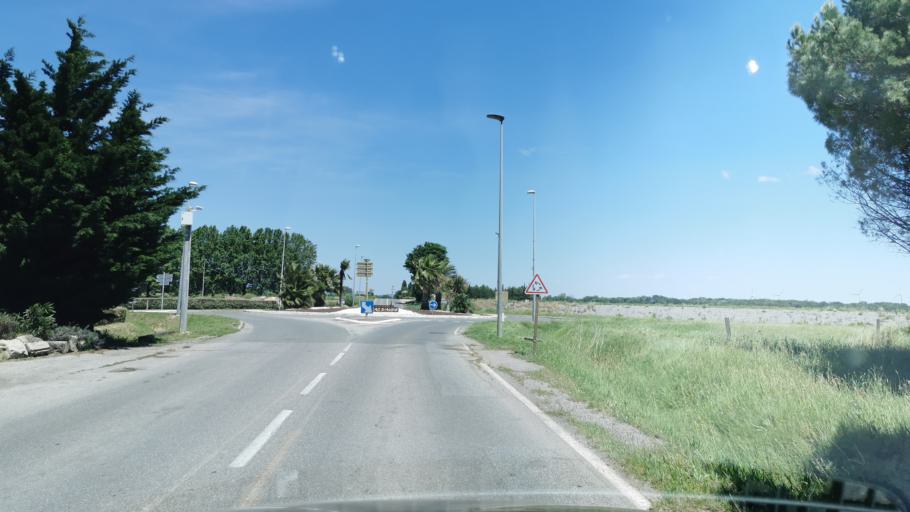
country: FR
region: Languedoc-Roussillon
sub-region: Departement de l'Aude
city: Ouveillan
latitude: 43.2505
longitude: 3.0028
